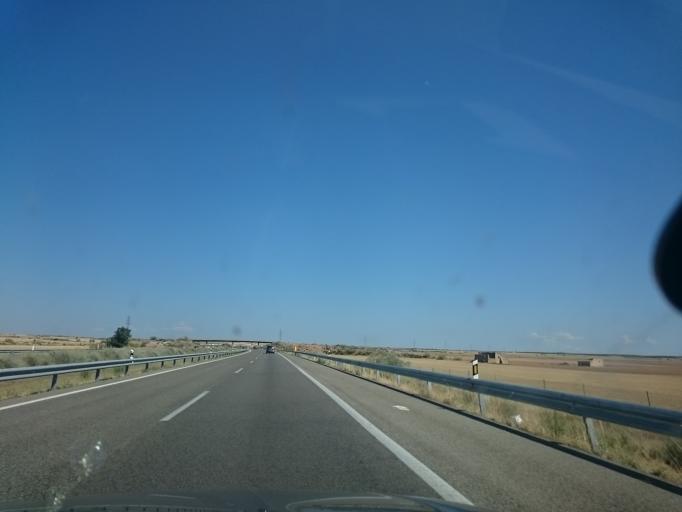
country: ES
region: Aragon
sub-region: Provincia de Zaragoza
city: Mequinensa / Mequinenza
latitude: 41.4722
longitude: 0.2157
